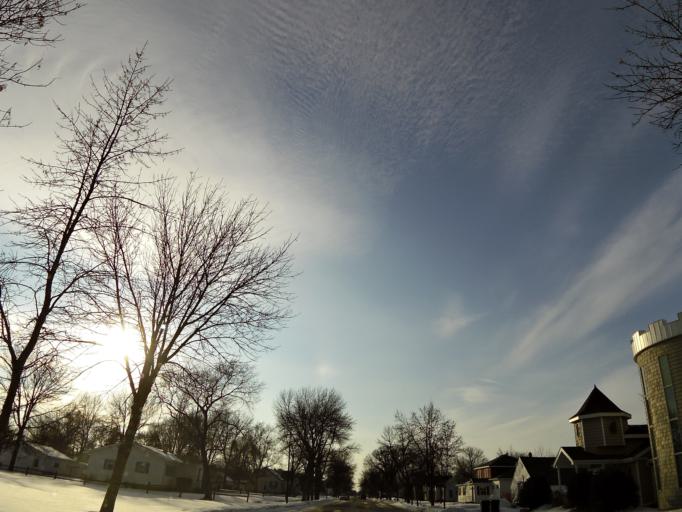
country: US
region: North Dakota
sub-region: Walsh County
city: Grafton
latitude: 48.4195
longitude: -97.3996
